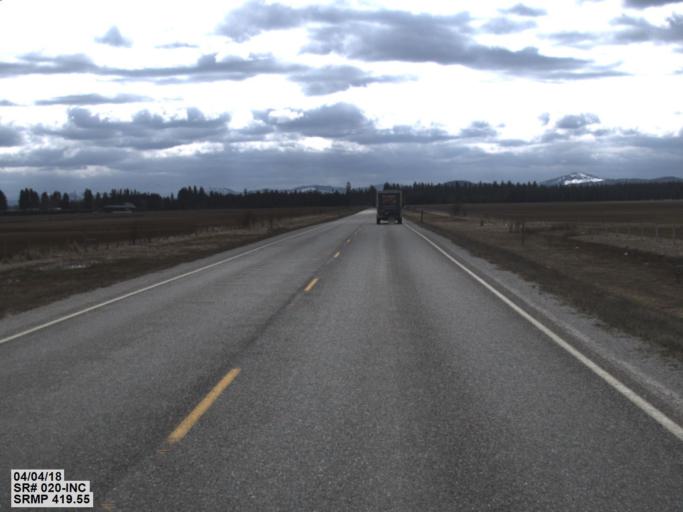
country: US
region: Washington
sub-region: Pend Oreille County
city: Newport
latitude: 48.3303
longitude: -117.3007
